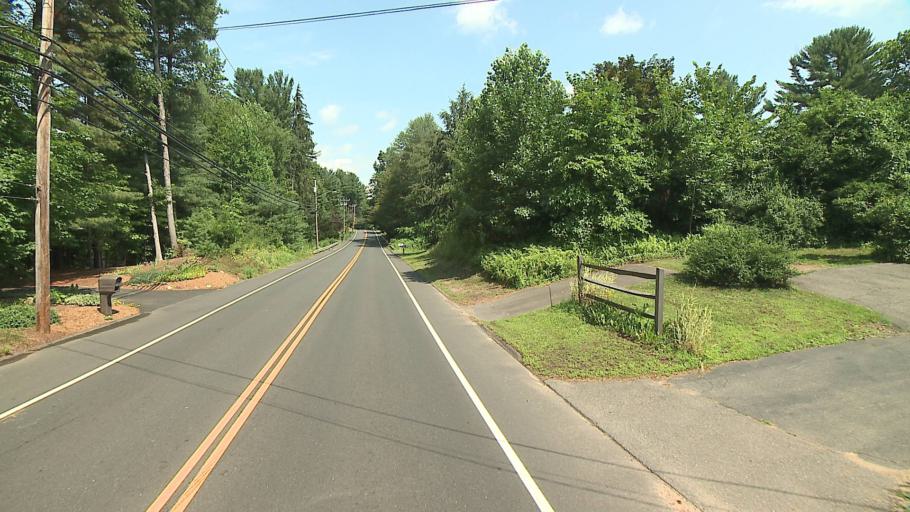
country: US
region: Connecticut
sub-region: Hartford County
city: Collinsville
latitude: 41.7896
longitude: -72.8928
